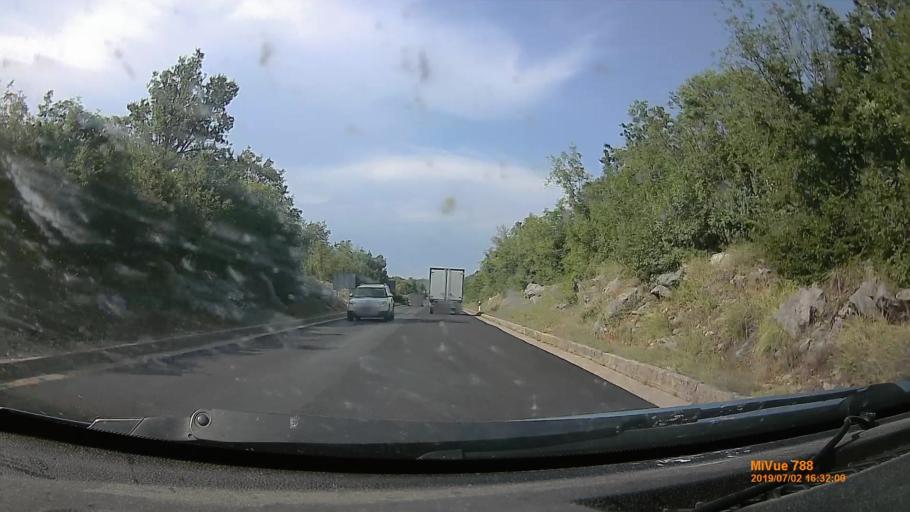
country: HR
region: Primorsko-Goranska
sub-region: Grad Krk
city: Krk
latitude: 45.0595
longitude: 14.4876
